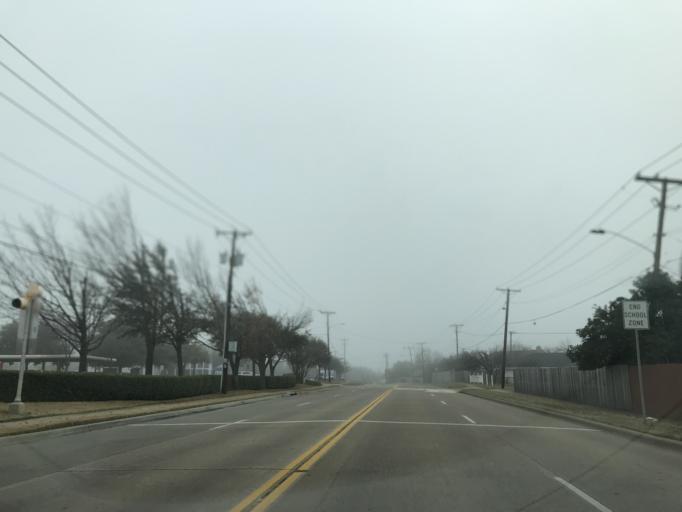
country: US
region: Texas
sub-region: Tarrant County
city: Arlington
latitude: 32.7742
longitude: -97.0787
